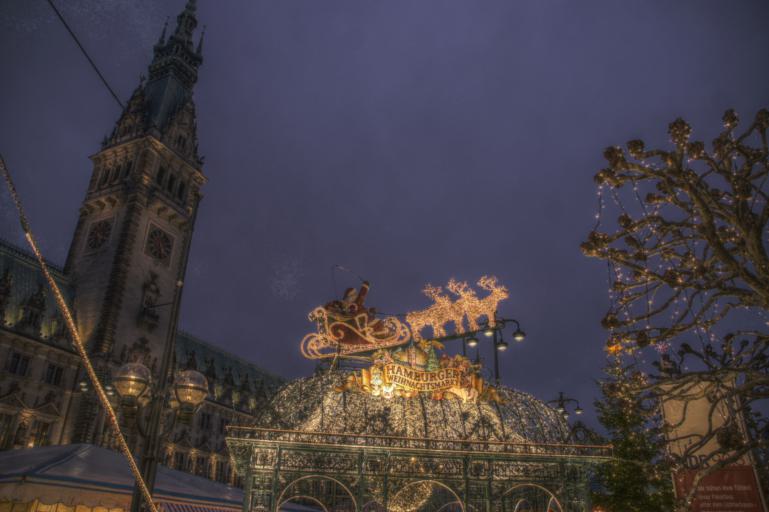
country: DE
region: Hamburg
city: Altstadt
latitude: 53.5505
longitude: 9.9937
